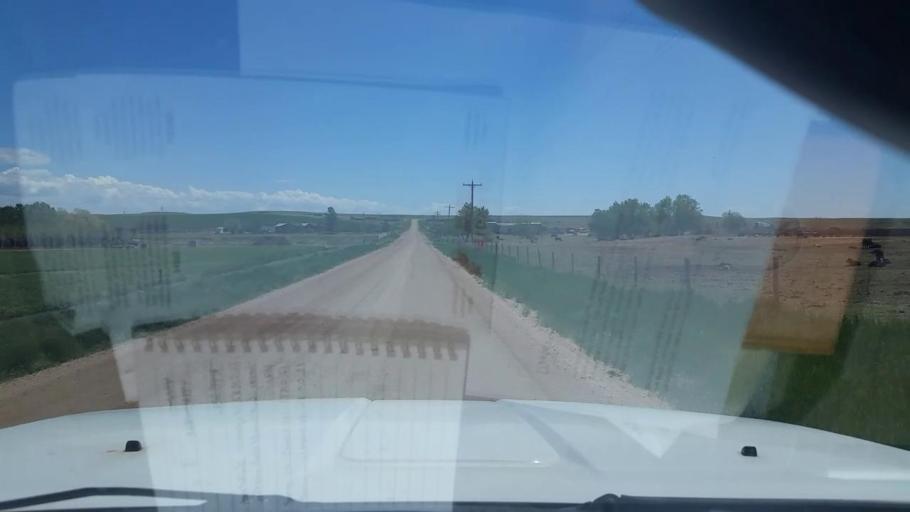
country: US
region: Colorado
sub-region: Larimer County
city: Wellington
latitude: 40.7981
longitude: -105.0514
